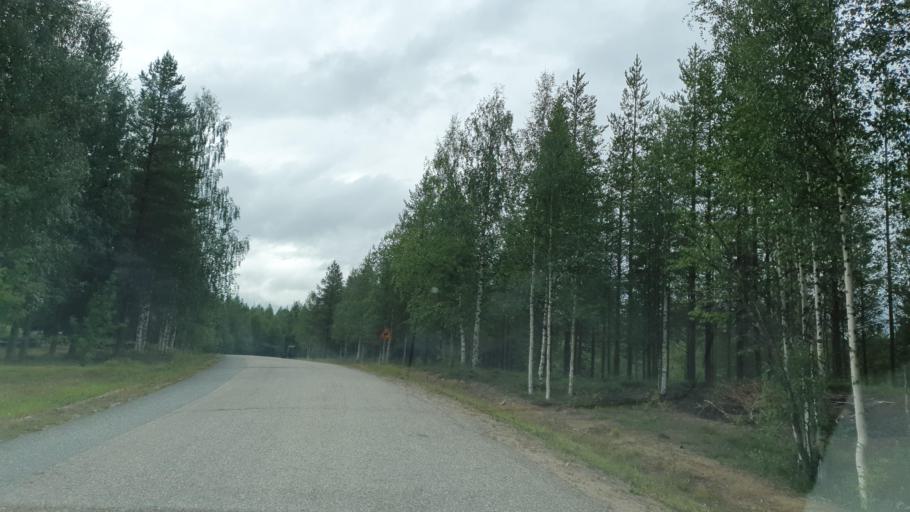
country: FI
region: Lapland
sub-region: Tunturi-Lappi
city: Kolari
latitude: 67.5042
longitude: 24.2604
